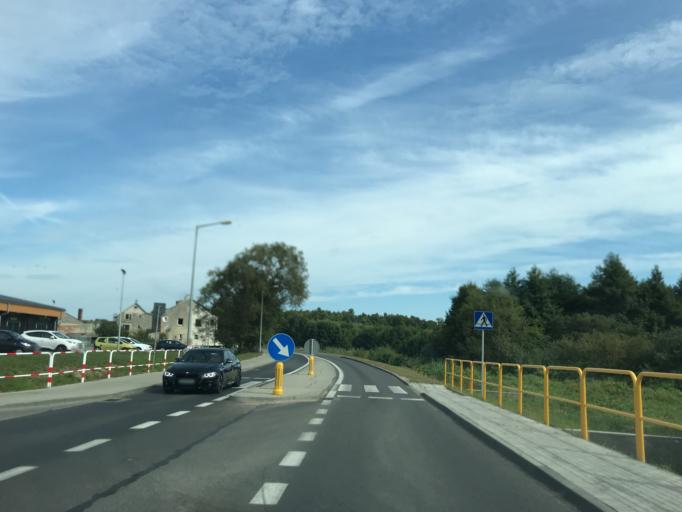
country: PL
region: Pomeranian Voivodeship
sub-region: Powiat pucki
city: Krokowa
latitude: 54.7796
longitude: 18.1670
